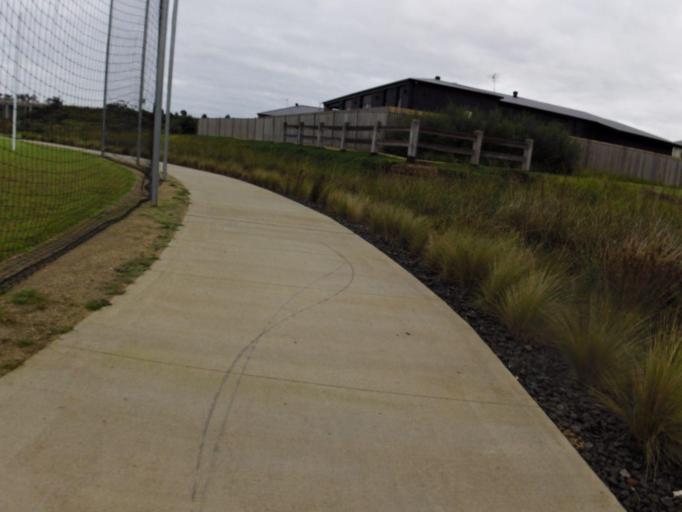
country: AU
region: Victoria
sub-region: Greater Geelong
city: Hamlyn Heights
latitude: -38.1339
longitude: 144.3130
